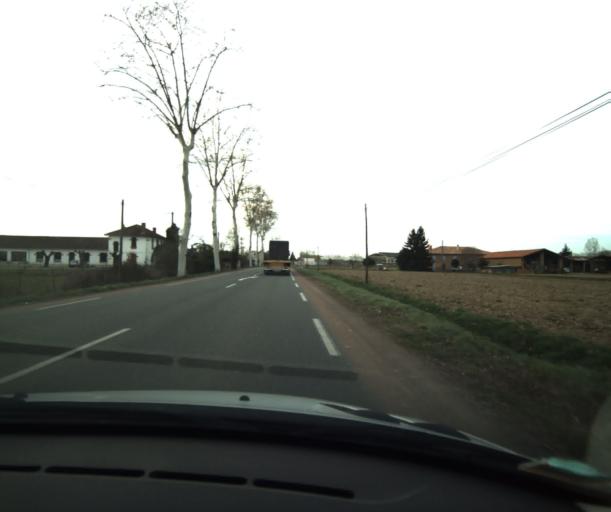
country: FR
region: Midi-Pyrenees
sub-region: Departement du Tarn-et-Garonne
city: Saint-Porquier
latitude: 44.0249
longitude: 1.1471
